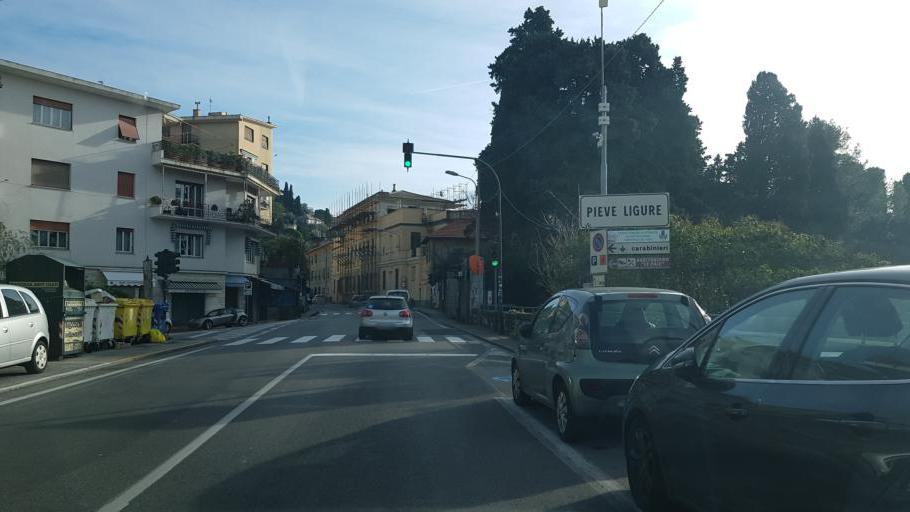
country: IT
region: Liguria
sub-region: Provincia di Genova
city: Bogliasco
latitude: 44.3776
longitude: 9.0771
